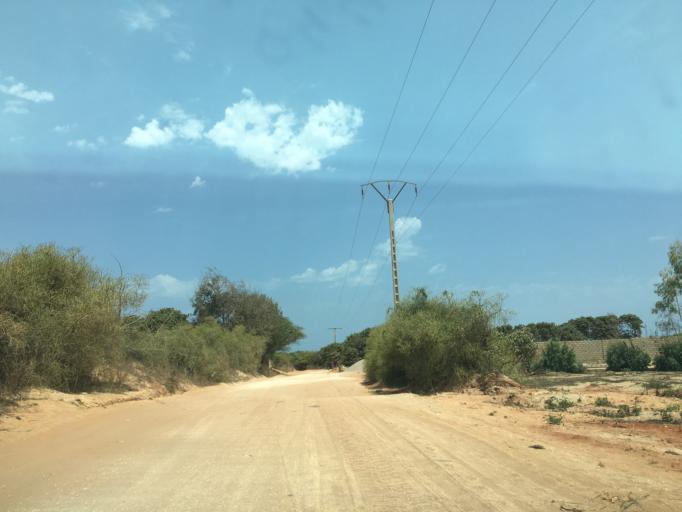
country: SN
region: Thies
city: Thies
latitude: 14.8164
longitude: -17.1961
